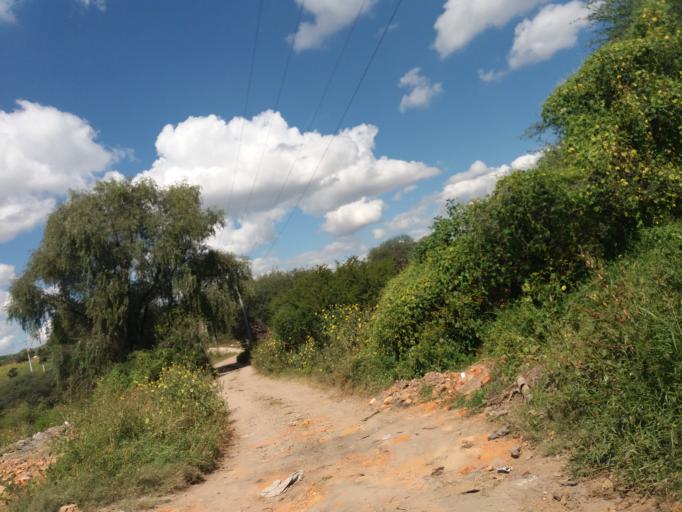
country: MX
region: Aguascalientes
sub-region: Aguascalientes
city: San Sebastian [Fraccionamiento]
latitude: 21.8073
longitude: -102.2418
